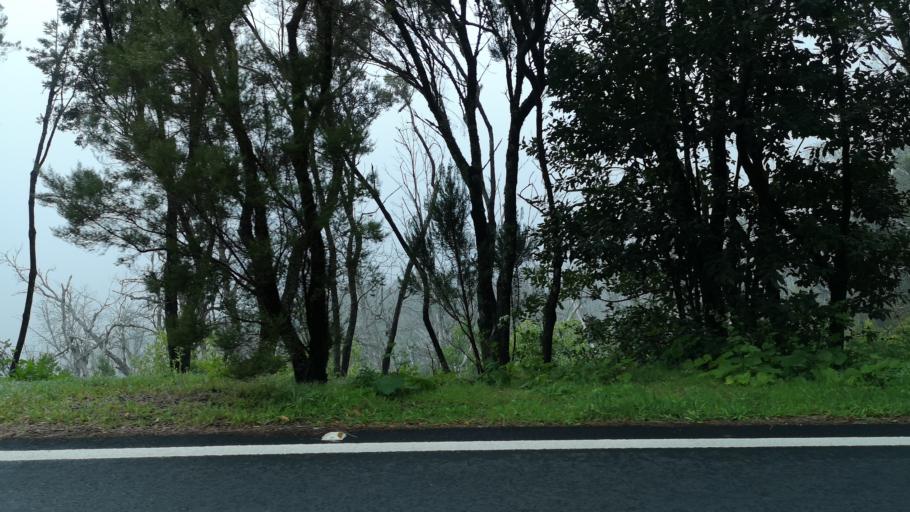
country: ES
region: Canary Islands
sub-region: Provincia de Santa Cruz de Tenerife
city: Alajero
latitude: 28.1194
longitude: -17.2478
